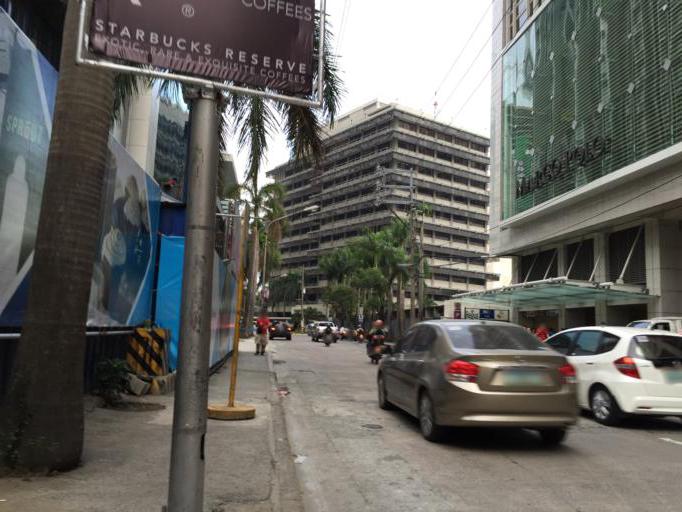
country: PH
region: Metro Manila
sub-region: Pasig
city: Pasig City
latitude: 14.5871
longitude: 121.0631
